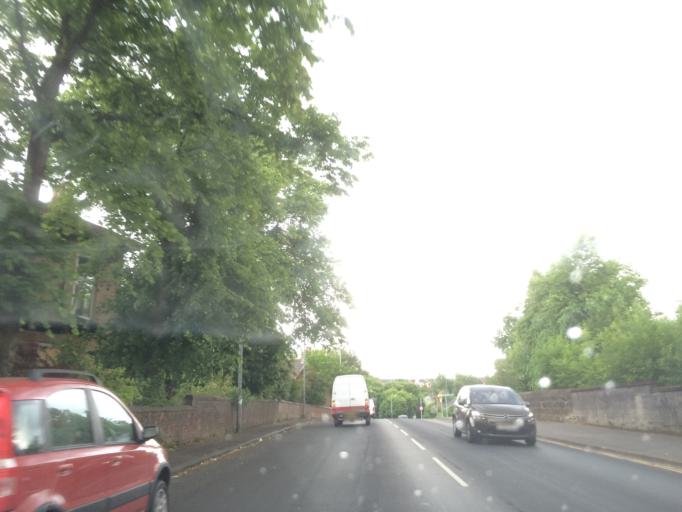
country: GB
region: Scotland
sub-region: Glasgow City
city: Glasgow
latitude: 55.8329
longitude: -4.2557
